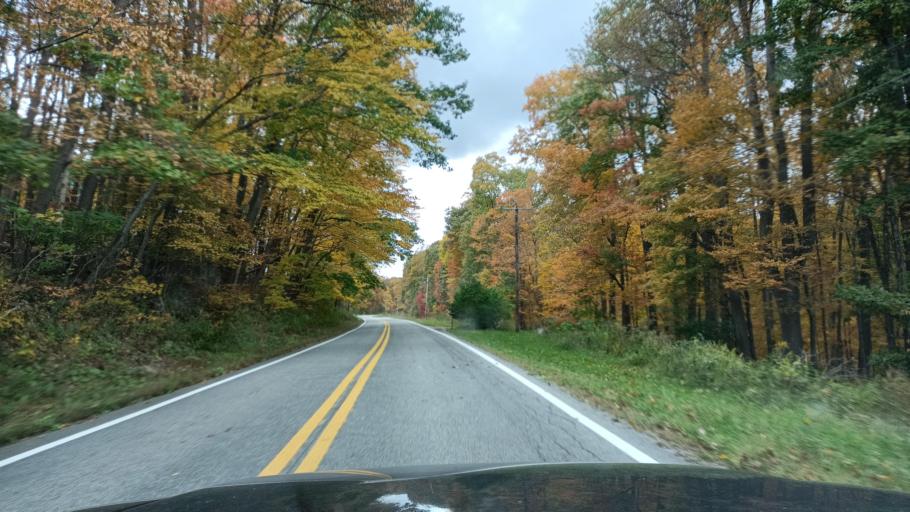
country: US
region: West Virginia
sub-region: Monongalia County
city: Cheat Lake
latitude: 39.6559
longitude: -79.7572
